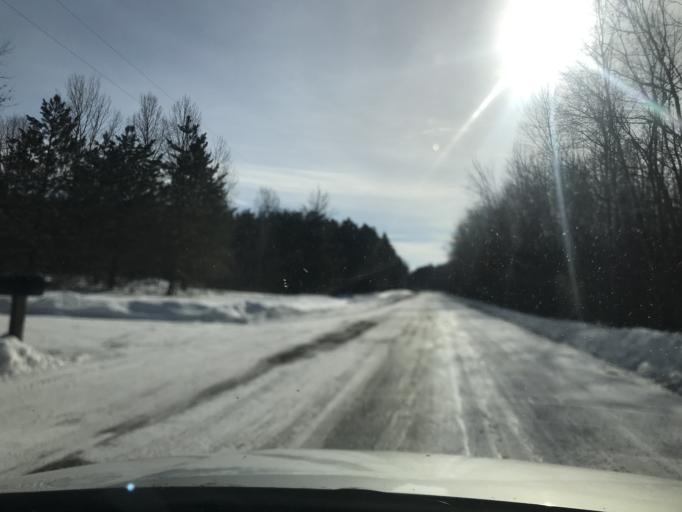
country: US
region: Wisconsin
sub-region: Oconto County
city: Gillett
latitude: 45.1240
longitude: -88.2499
